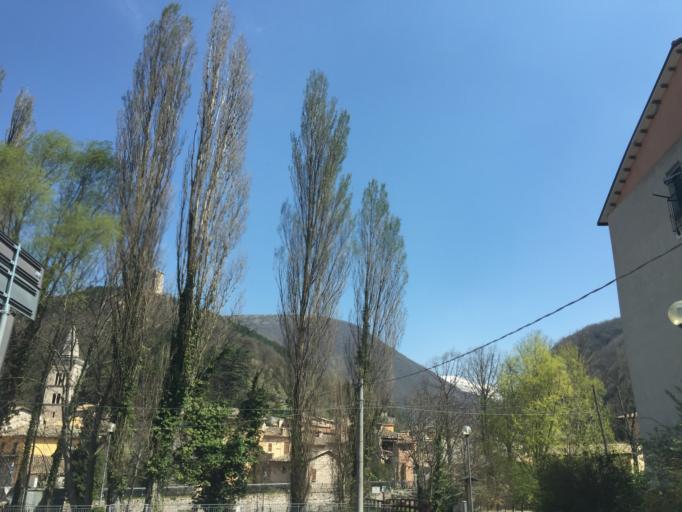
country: IT
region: The Marches
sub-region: Provincia di Macerata
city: Visso
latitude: 42.9301
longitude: 13.0865
